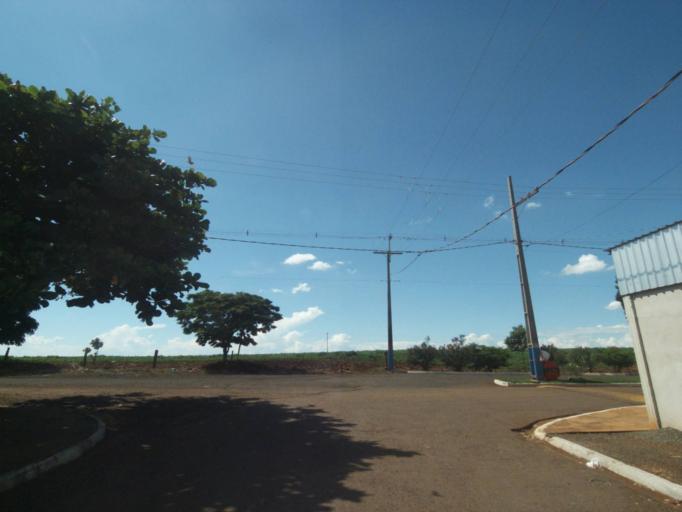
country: BR
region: Parana
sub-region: Sertanopolis
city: Sertanopolis
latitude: -23.0453
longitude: -50.8241
